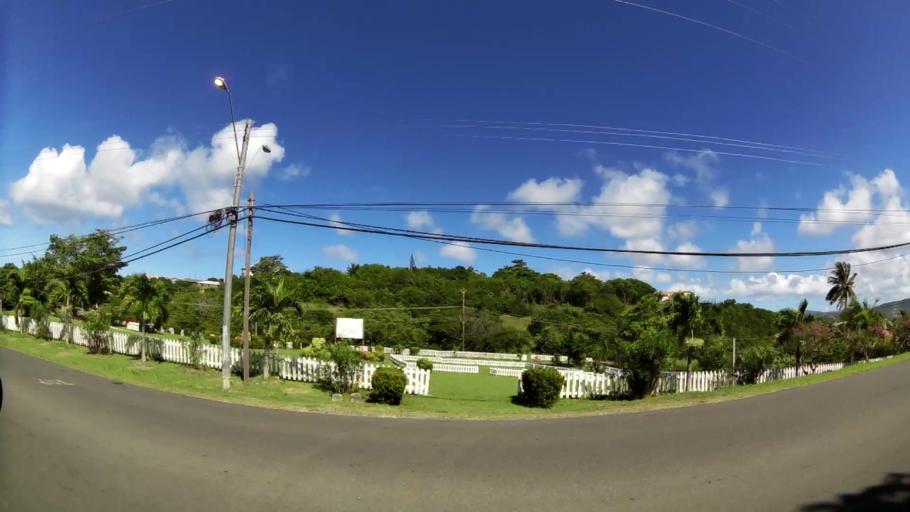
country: TT
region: Tobago
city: Scarborough
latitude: 11.1708
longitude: -60.7593
